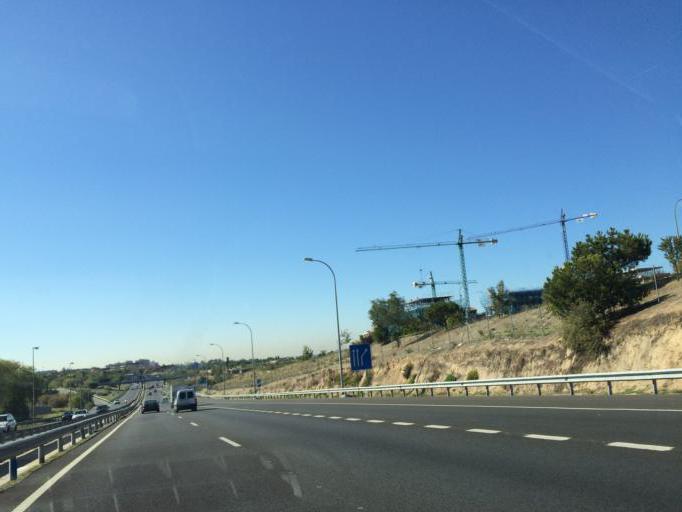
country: ES
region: Madrid
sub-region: Provincia de Madrid
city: Las Tablas
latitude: 40.5055
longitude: -3.6929
